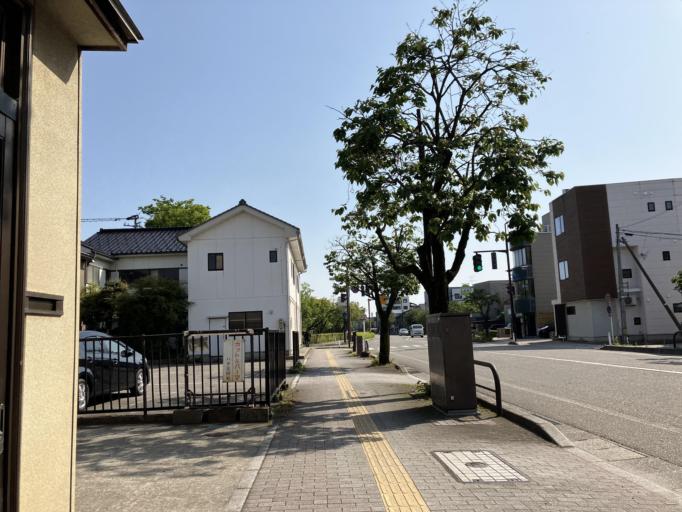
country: JP
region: Toyama
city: Takaoka
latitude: 36.7453
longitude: 137.0207
